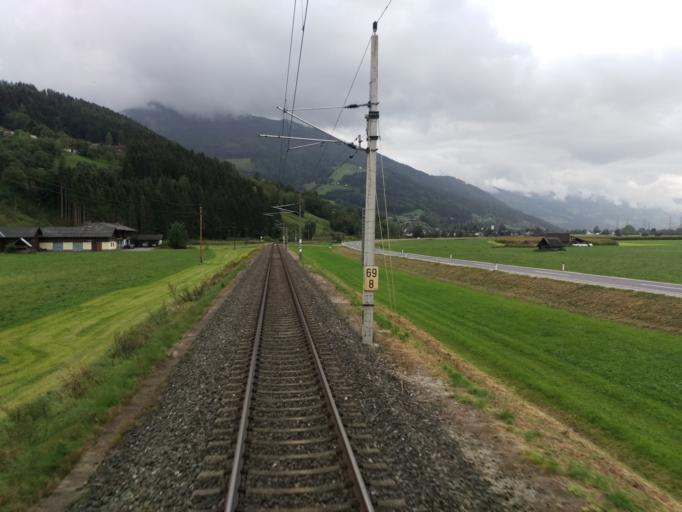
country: AT
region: Styria
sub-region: Politischer Bezirk Liezen
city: Niederoblarn
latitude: 47.4720
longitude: 14.0081
